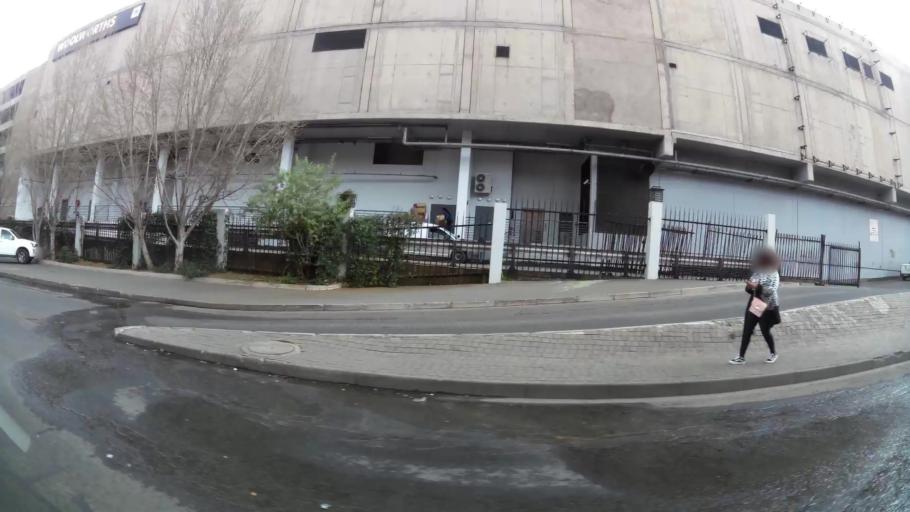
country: ZA
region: Orange Free State
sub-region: Mangaung Metropolitan Municipality
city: Bloemfontein
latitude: -29.1155
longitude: 26.2115
